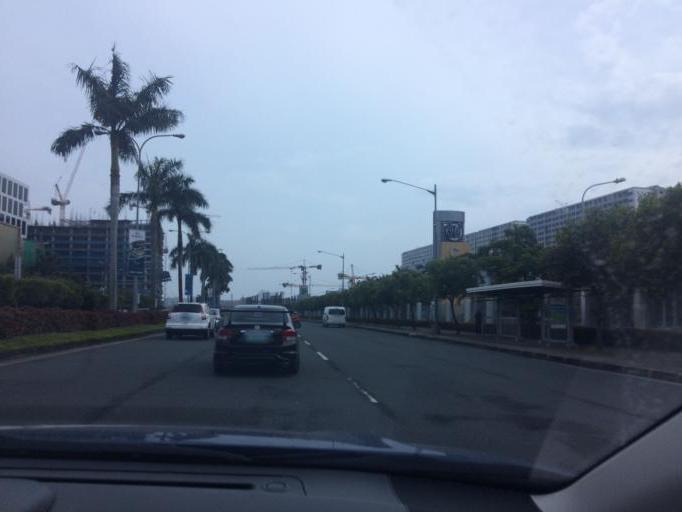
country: PH
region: Metro Manila
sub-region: City of Manila
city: Port Area
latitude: 14.5374
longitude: 120.9842
